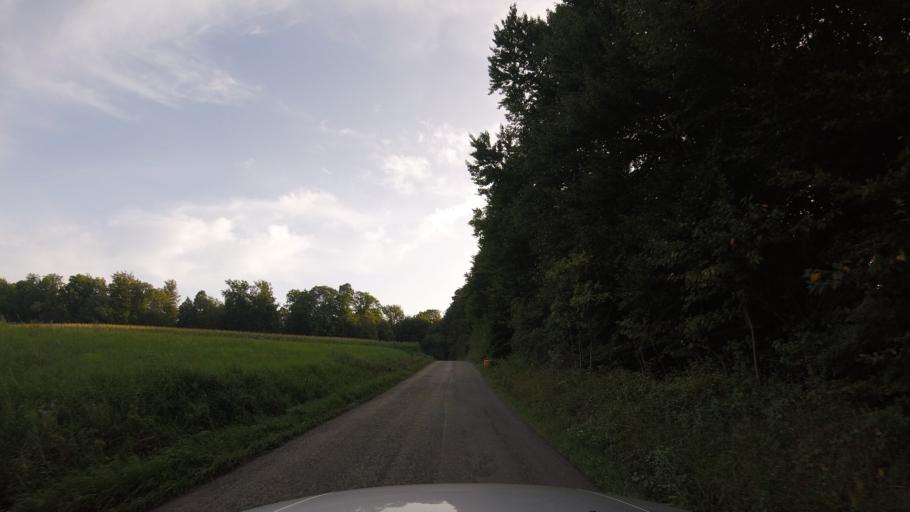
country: DE
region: Baden-Wuerttemberg
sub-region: Regierungsbezirk Stuttgart
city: Aspach
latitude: 49.0062
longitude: 9.3879
